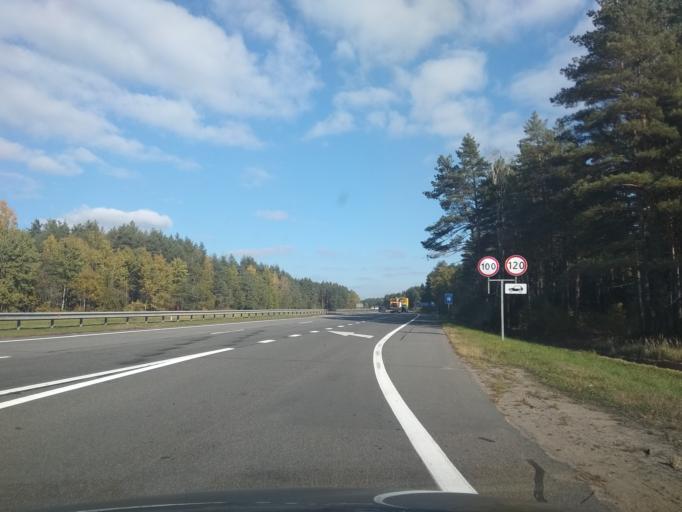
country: BY
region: Brest
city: Baranovichi
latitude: 53.0531
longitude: 25.8560
